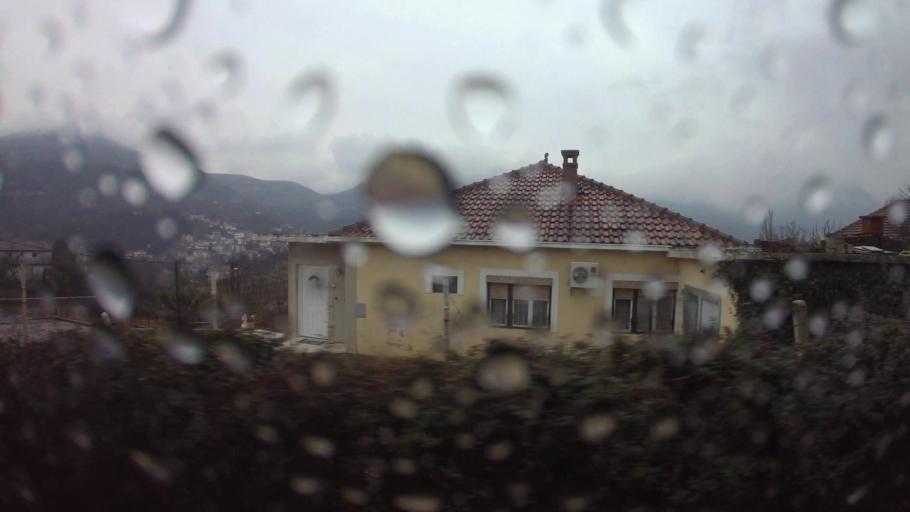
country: BA
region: Federation of Bosnia and Herzegovina
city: Cim
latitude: 43.3476
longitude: 17.7814
